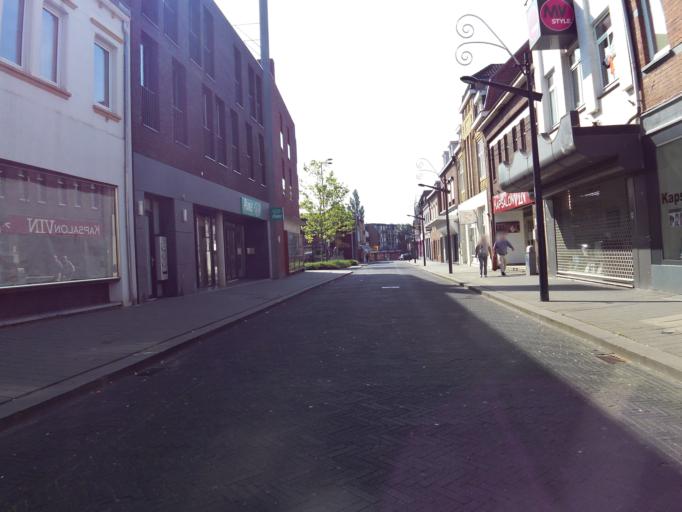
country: NL
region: Limburg
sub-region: Gemeente Kerkrade
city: Kerkrade
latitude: 50.8575
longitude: 6.0261
